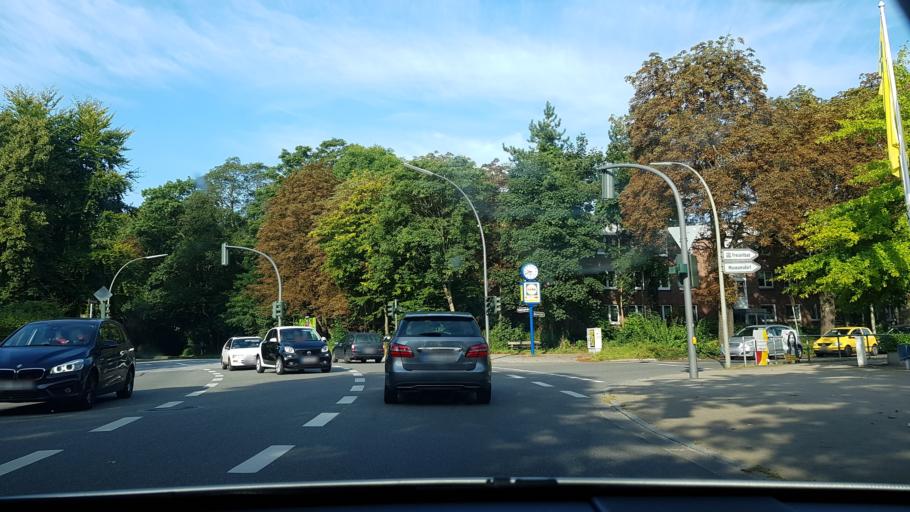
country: DE
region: Hamburg
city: Bergstedt
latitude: 53.6476
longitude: 10.1689
